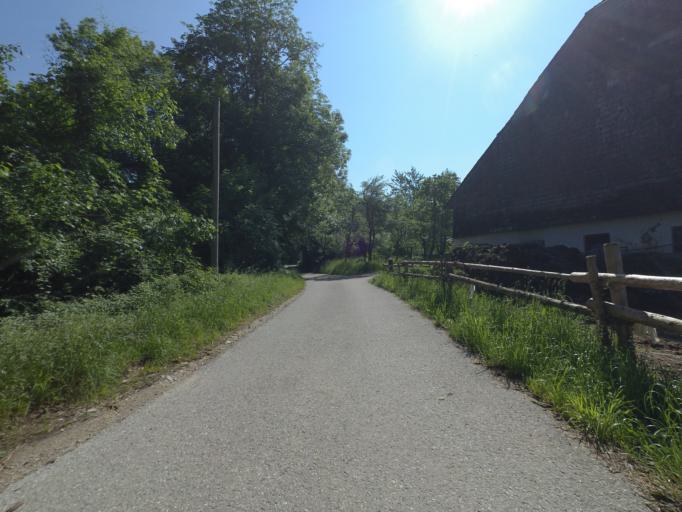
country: DE
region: Bavaria
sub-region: Upper Bavaria
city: Piding
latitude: 47.7375
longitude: 12.9351
